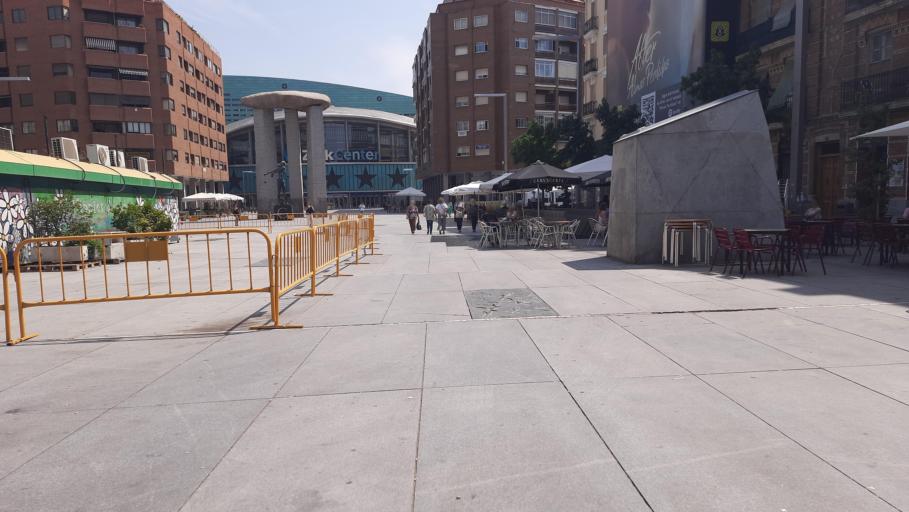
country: ES
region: Madrid
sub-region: Provincia de Madrid
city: Salamanca
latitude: 40.4239
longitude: -3.6742
